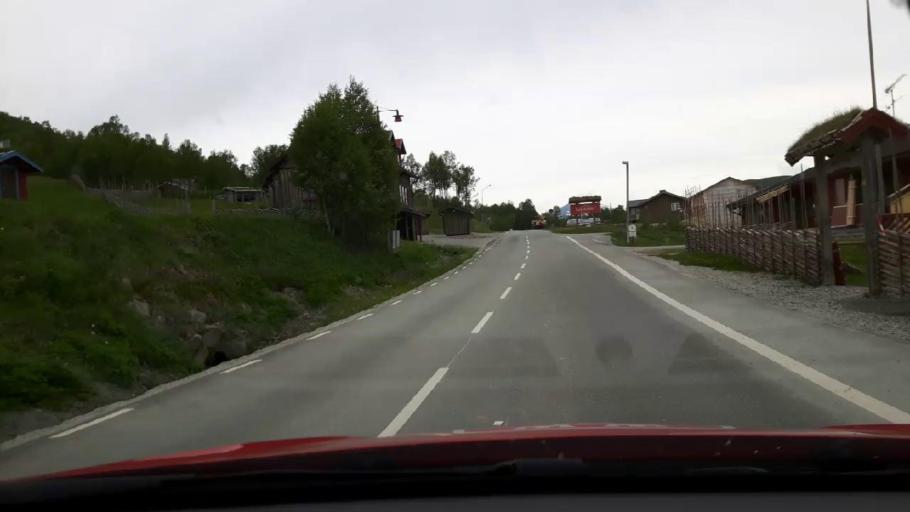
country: NO
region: Sor-Trondelag
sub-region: Tydal
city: Aas
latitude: 62.7021
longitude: 12.3871
